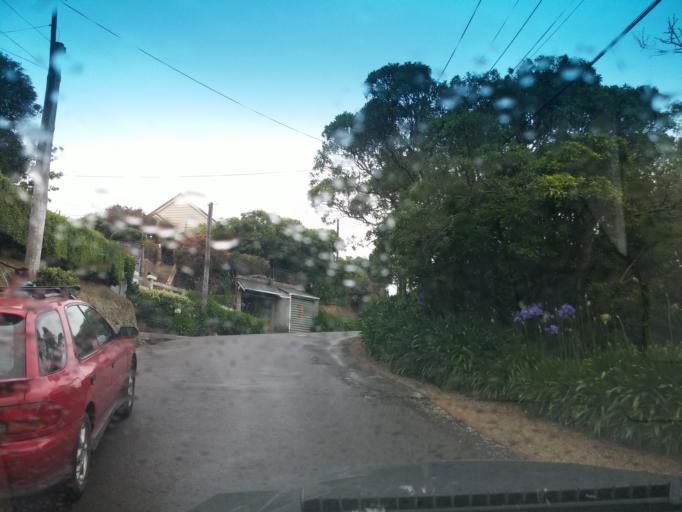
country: NZ
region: Wellington
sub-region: Wellington City
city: Kelburn
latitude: -41.2851
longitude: 174.7556
